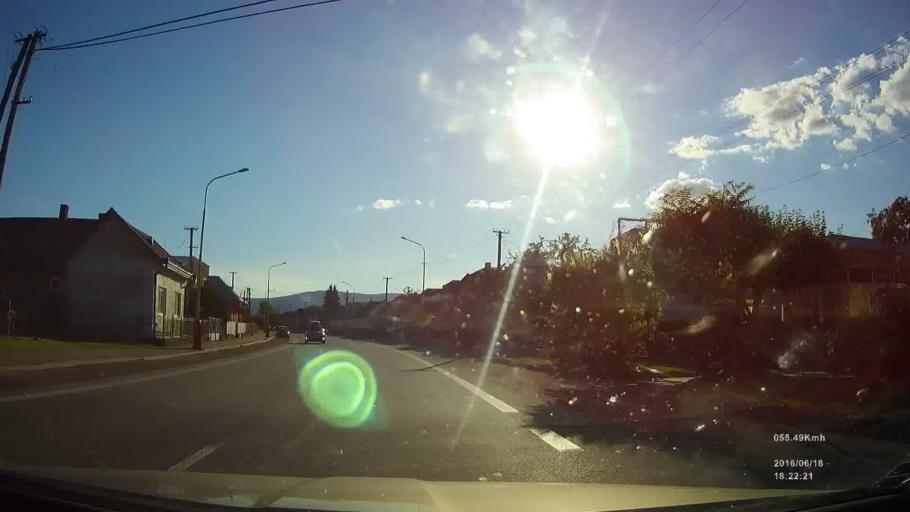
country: SK
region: Kosicky
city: Secovce
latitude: 48.7036
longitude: 21.6782
